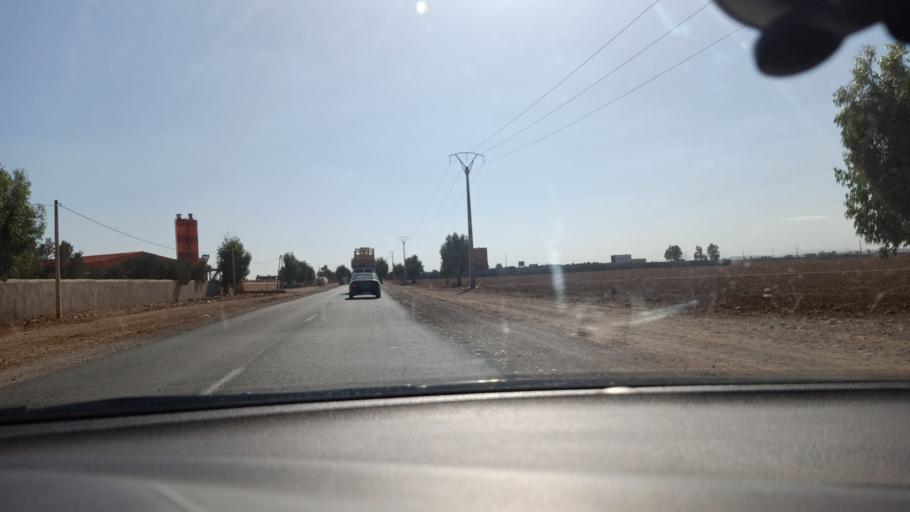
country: MA
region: Doukkala-Abda
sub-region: Safi
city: Youssoufia
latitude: 32.1032
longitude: -8.6117
